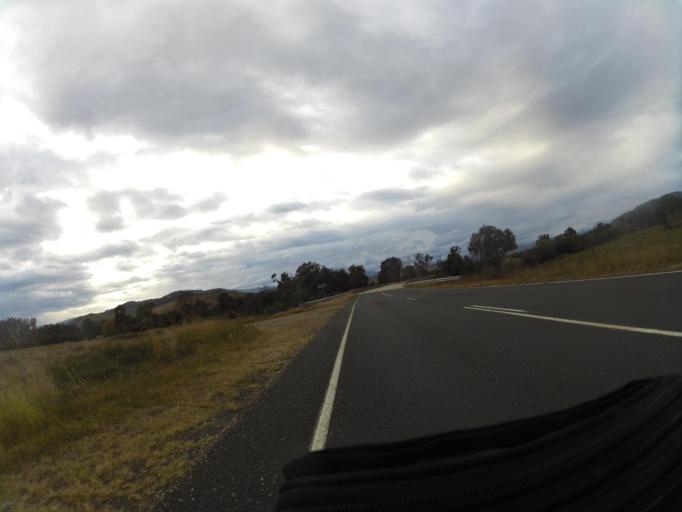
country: AU
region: New South Wales
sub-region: Snowy River
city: Jindabyne
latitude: -36.0906
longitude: 147.9795
